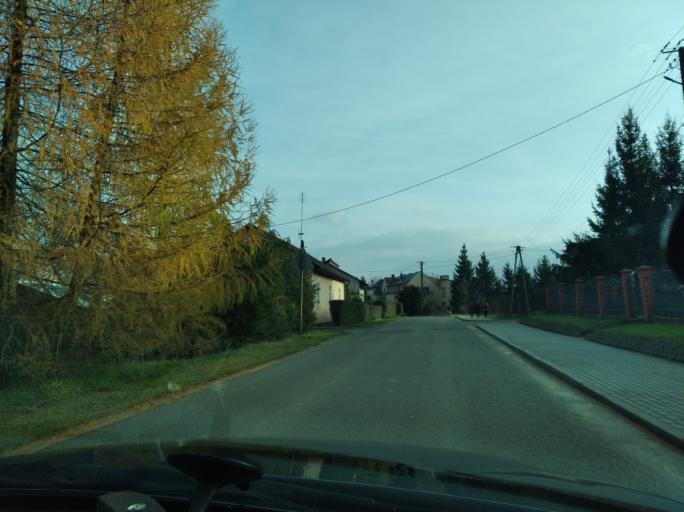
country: PL
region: Subcarpathian Voivodeship
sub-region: Powiat przeworski
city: Siedleczka
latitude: 49.9603
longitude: 22.3797
